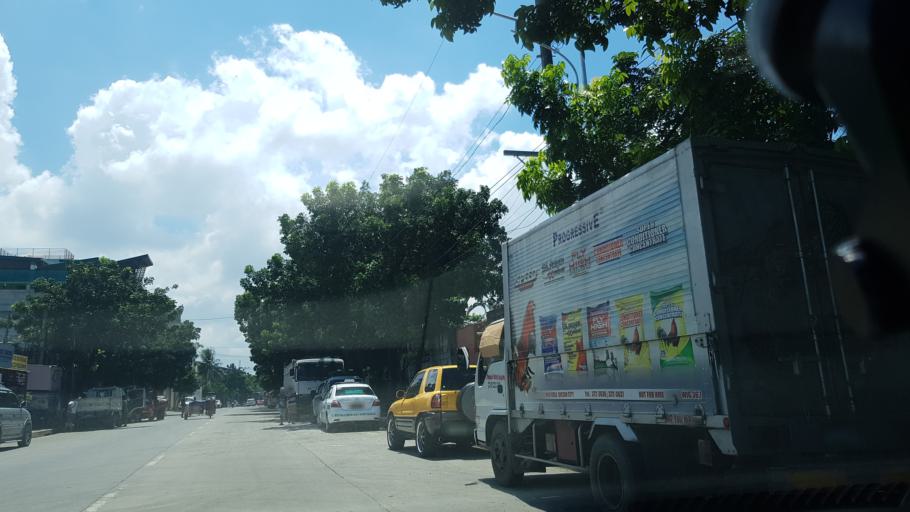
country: PH
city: Sambayanihan People's Village
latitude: 14.4650
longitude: 120.9962
